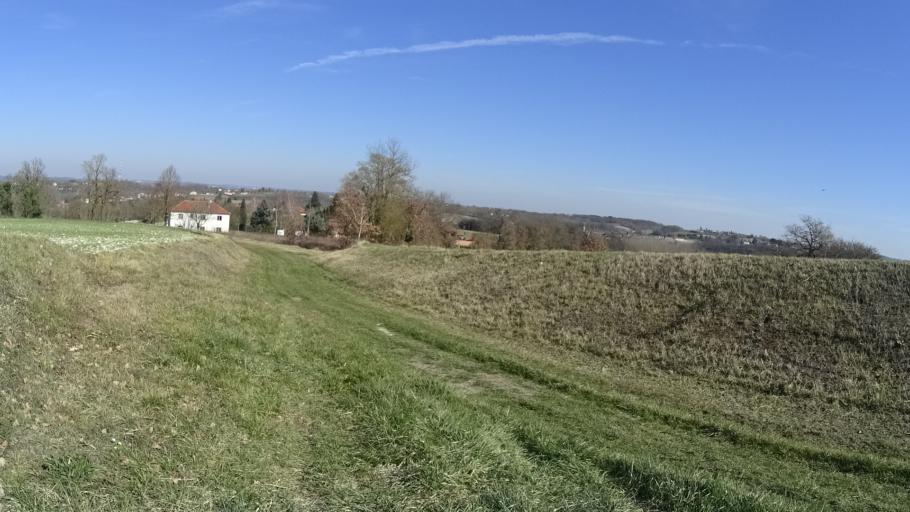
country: FR
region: Aquitaine
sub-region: Departement de la Dordogne
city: Riberac
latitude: 45.2258
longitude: 0.3446
